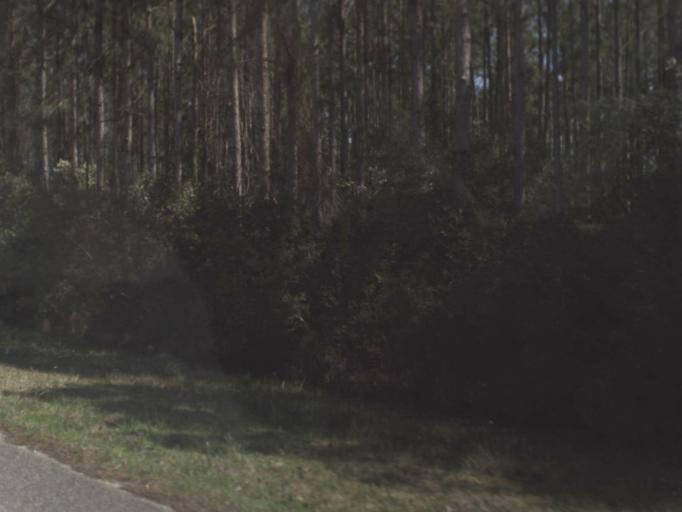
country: US
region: Florida
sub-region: Franklin County
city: Apalachicola
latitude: 29.7242
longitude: -85.0930
